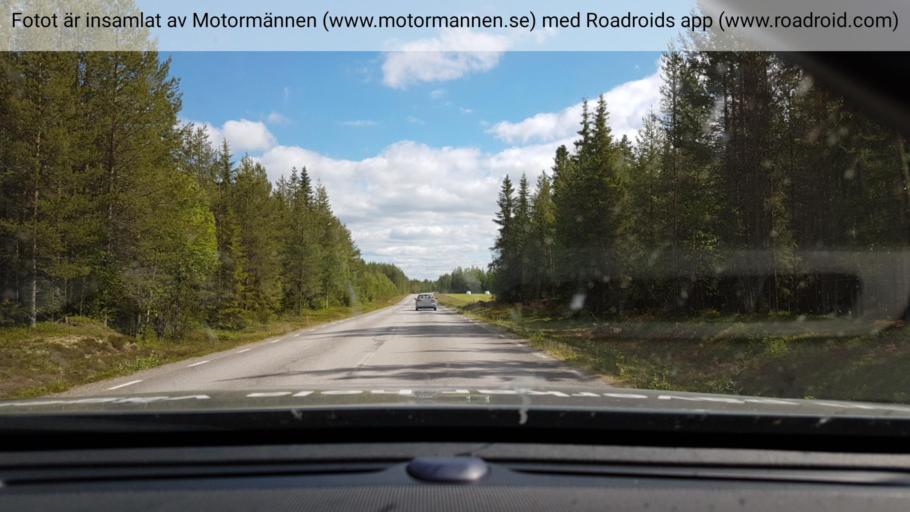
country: SE
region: Vaesterbotten
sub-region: Sorsele Kommun
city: Sorsele
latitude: 65.5965
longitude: 17.5000
